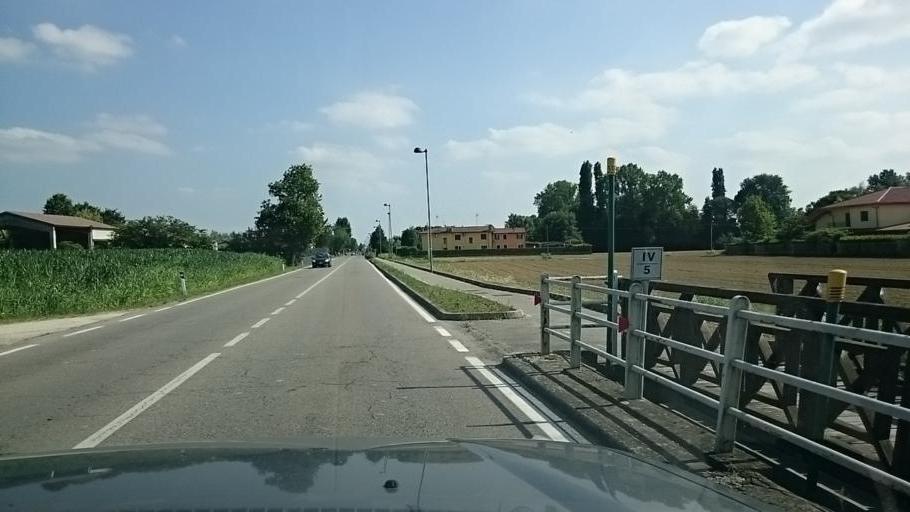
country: IT
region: Veneto
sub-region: Provincia di Padova
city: Abbazia Pisani
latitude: 45.5994
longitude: 11.8560
